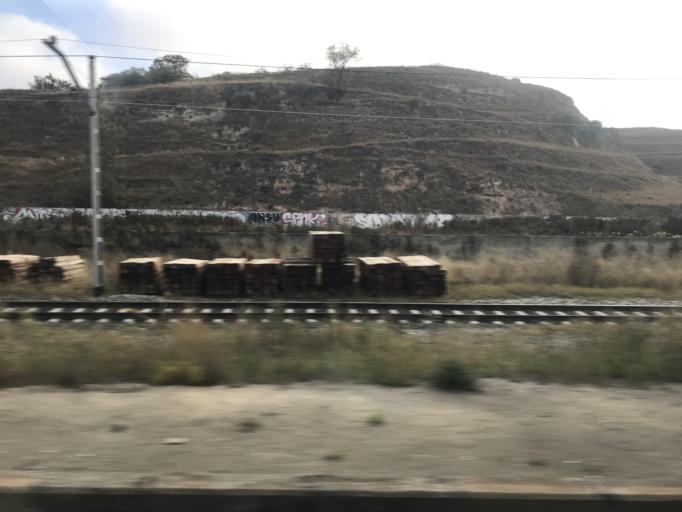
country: ES
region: Castille and Leon
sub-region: Provincia de Burgos
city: Briviesca
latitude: 42.5442
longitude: -3.3189
